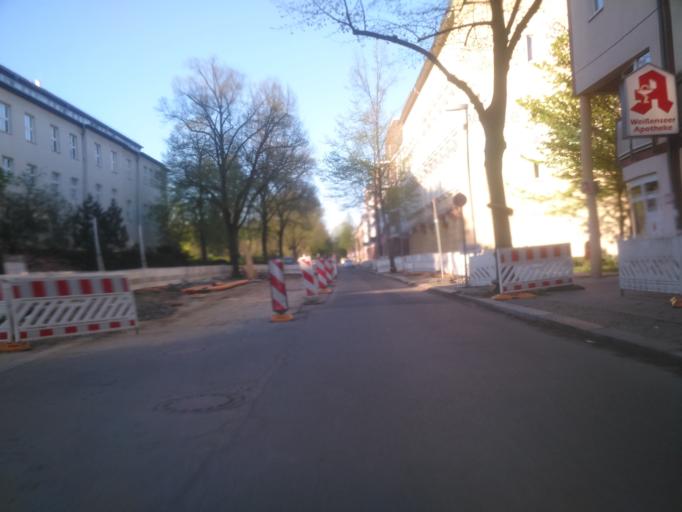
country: DE
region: Berlin
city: Weissensee
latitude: 52.5538
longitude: 13.4505
